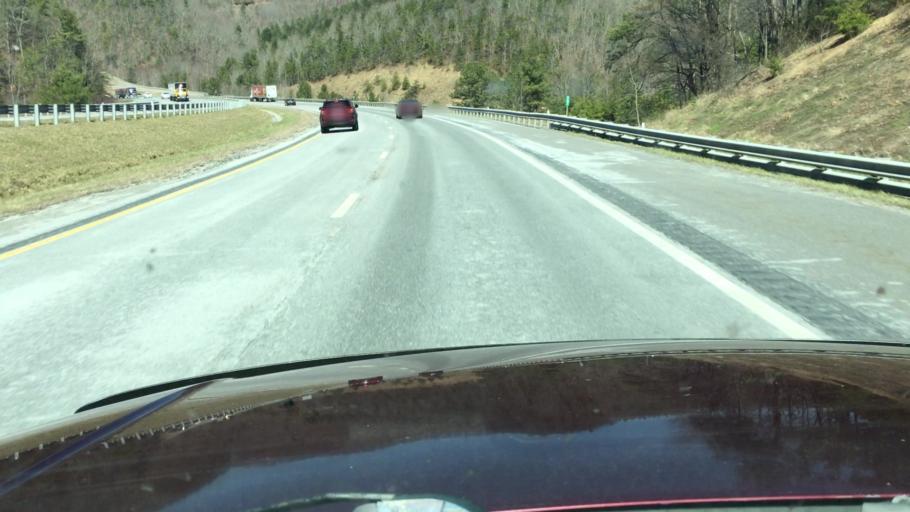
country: US
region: Virginia
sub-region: Bland County
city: Bland
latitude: 37.1365
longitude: -81.1220
